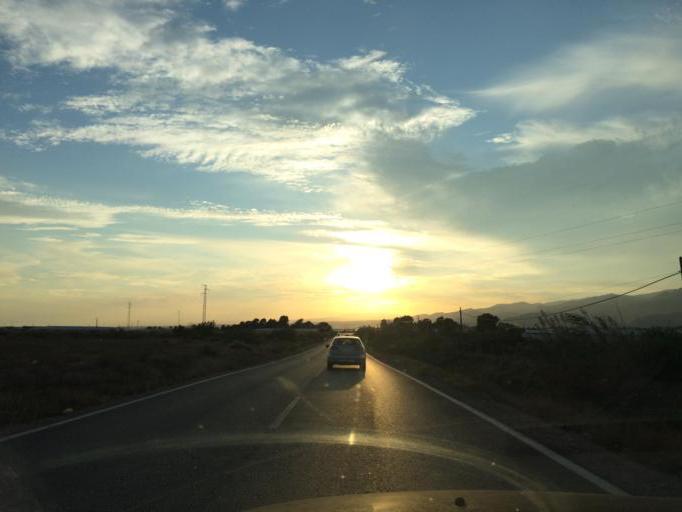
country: ES
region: Andalusia
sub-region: Provincia de Almeria
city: Nijar
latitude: 36.9324
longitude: -2.1131
